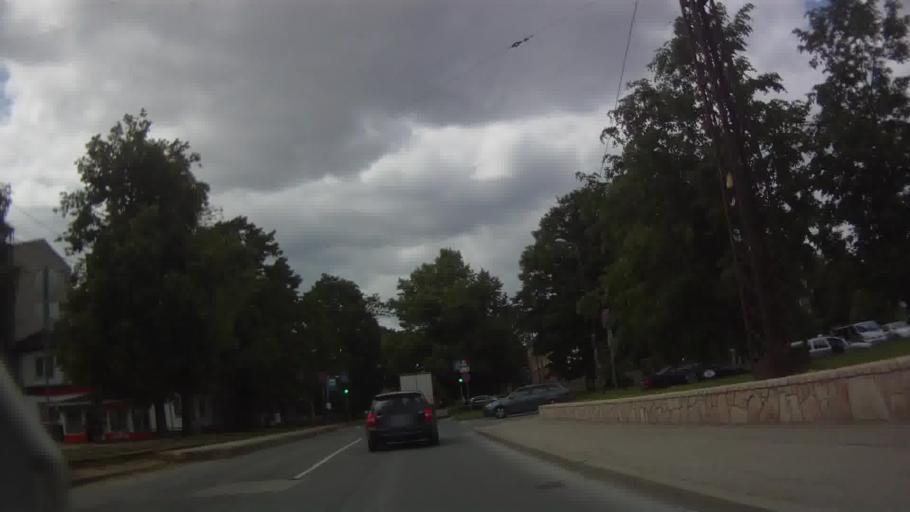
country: LV
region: Riga
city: Riga
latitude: 56.9150
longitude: 24.1126
